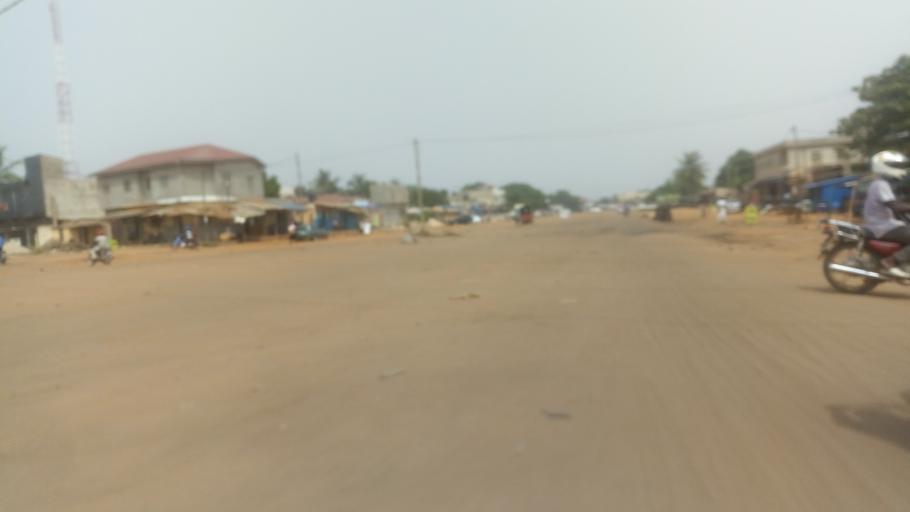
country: TG
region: Maritime
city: Lome
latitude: 6.1953
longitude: 1.1782
